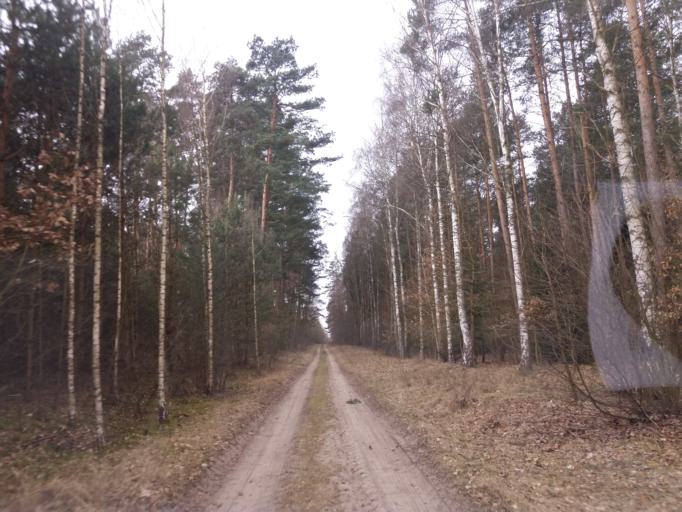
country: PL
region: West Pomeranian Voivodeship
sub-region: Powiat choszczenski
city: Recz
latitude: 53.1459
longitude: 15.5984
